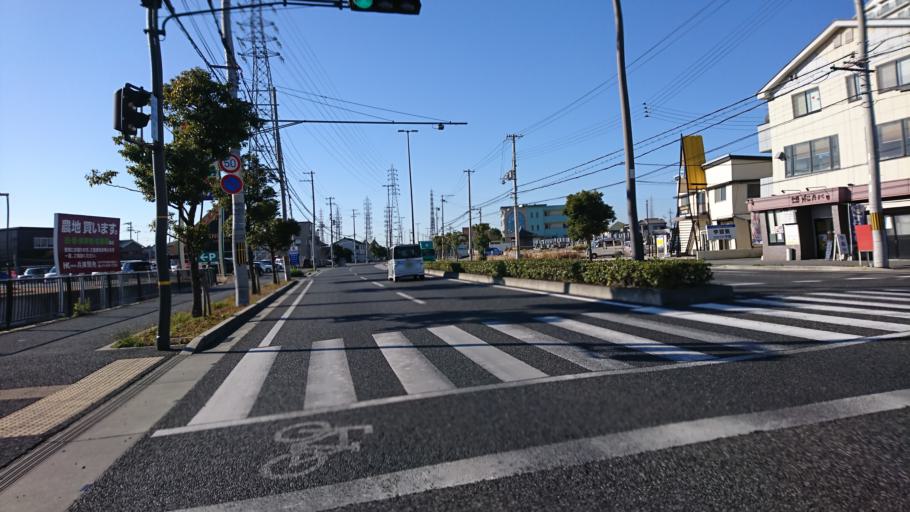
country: JP
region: Hyogo
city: Kakogawacho-honmachi
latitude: 34.7734
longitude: 134.8109
